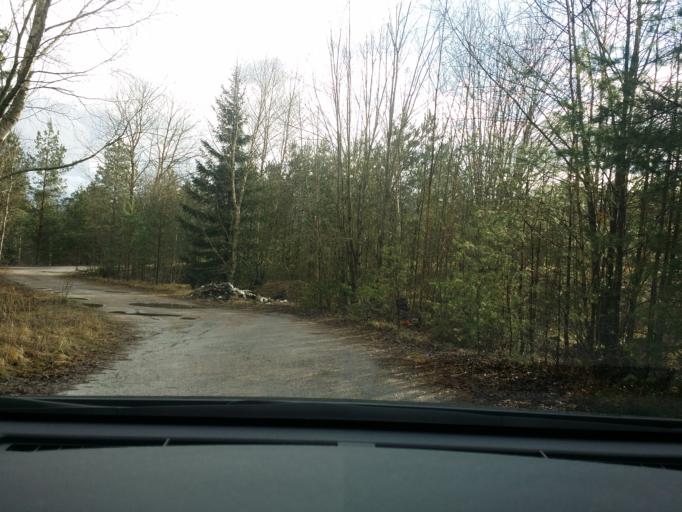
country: SE
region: Soedermanland
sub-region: Eskilstuna Kommun
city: Arla
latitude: 59.3254
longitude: 16.6826
